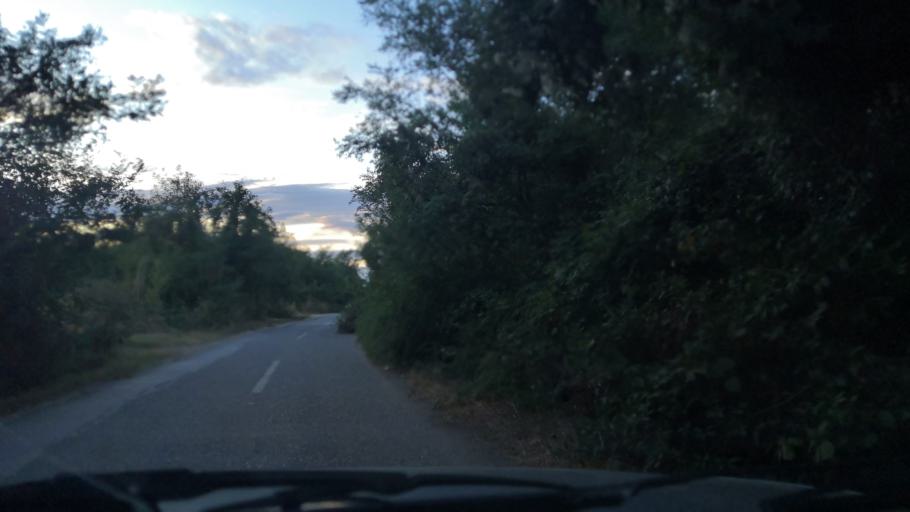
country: RO
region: Mehedinti
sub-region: Comuna Gruia
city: Izvoarele
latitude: 44.2829
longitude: 22.6388
